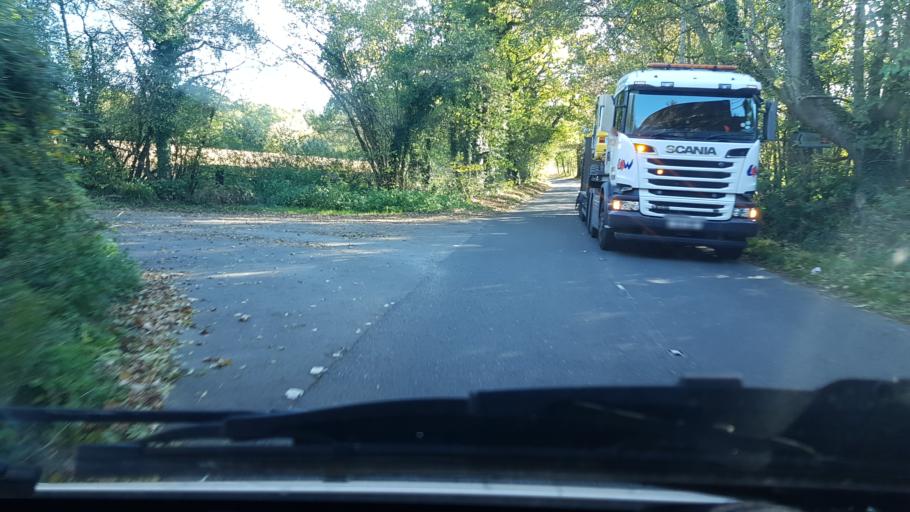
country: GB
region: England
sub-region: Surrey
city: Ockley
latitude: 51.1505
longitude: -0.3364
